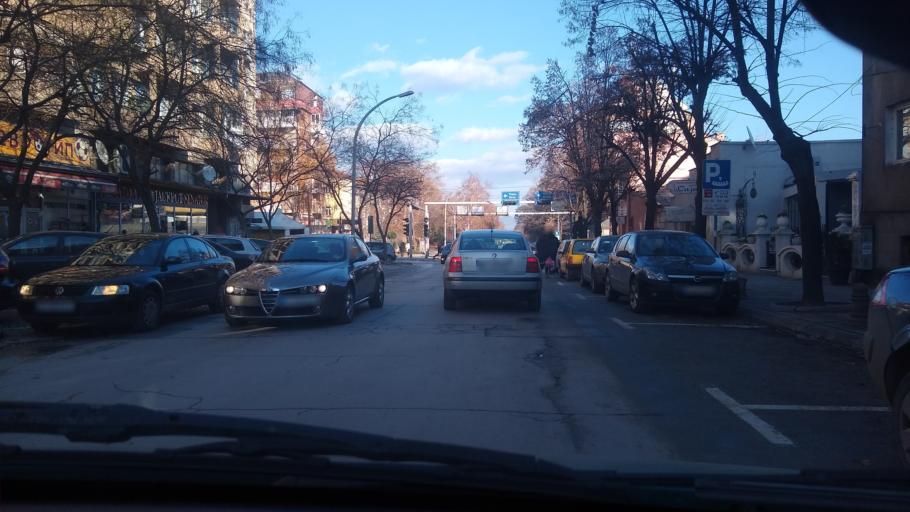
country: MK
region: Bitola
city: Bitola
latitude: 41.0281
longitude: 21.3370
